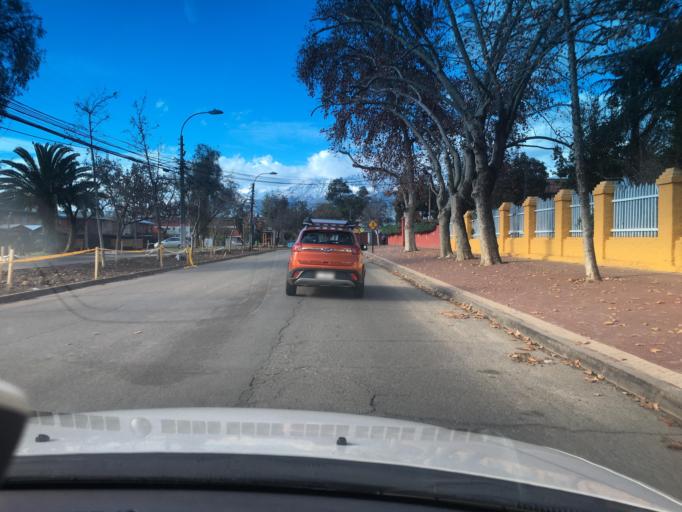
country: CL
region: Santiago Metropolitan
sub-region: Provincia de Santiago
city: Villa Presidente Frei, Nunoa, Santiago, Chile
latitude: -33.5160
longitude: -70.5896
